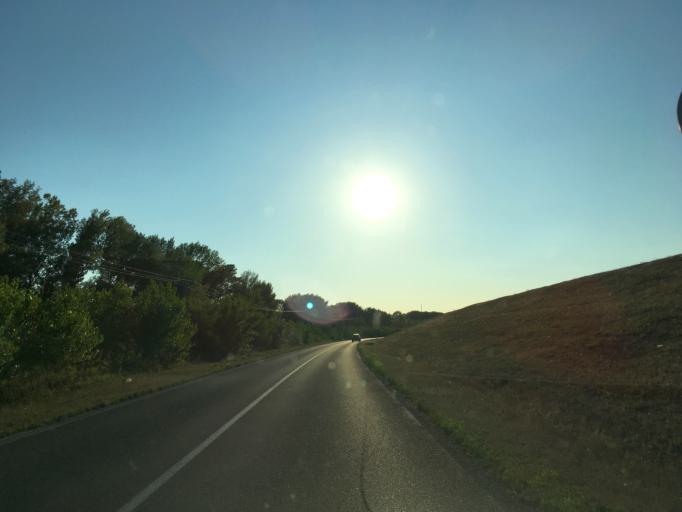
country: SK
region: Trnavsky
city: Samorin
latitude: 47.9958
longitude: 17.2762
